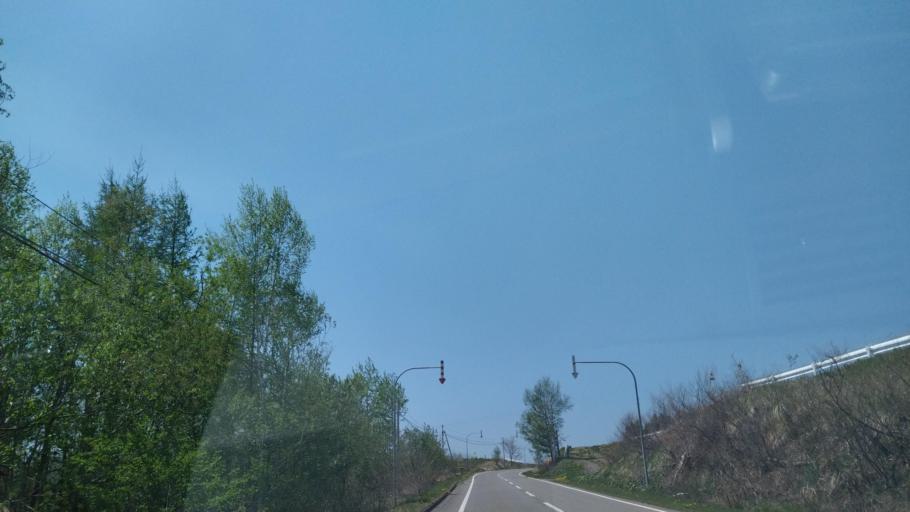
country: JP
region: Hokkaido
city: Obihiro
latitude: 42.9037
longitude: 143.0045
